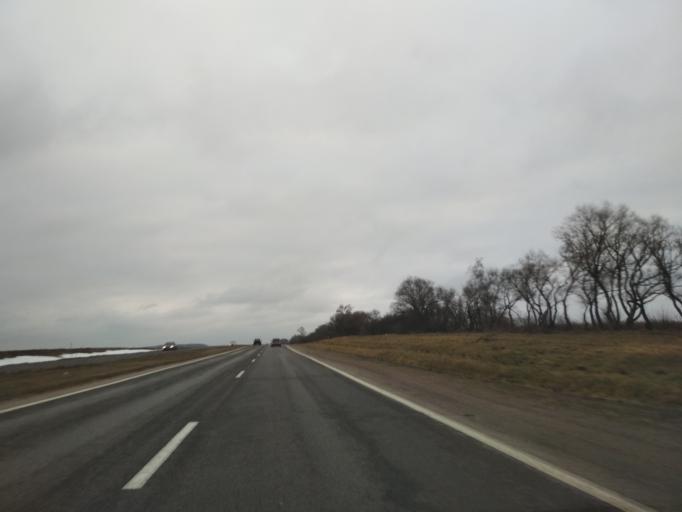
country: BY
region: Minsk
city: Blon'
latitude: 53.5656
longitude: 28.1415
